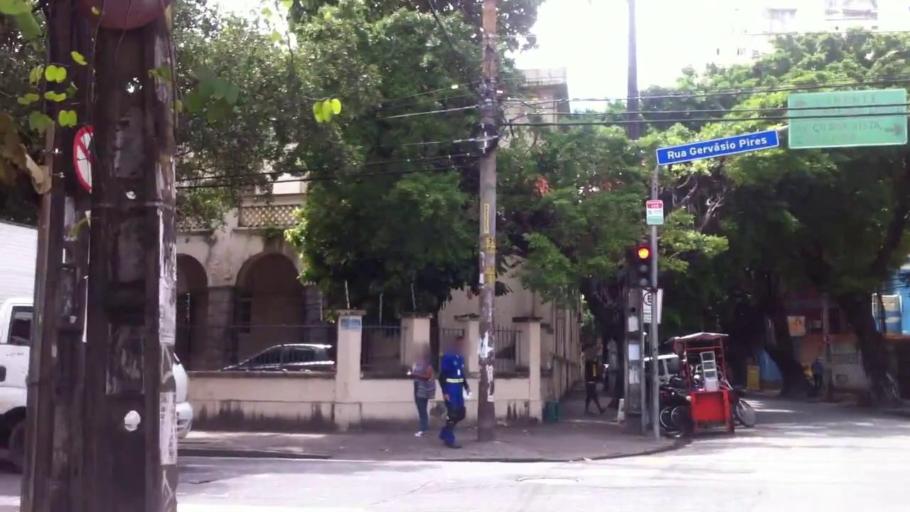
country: BR
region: Pernambuco
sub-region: Recife
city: Recife
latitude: -8.0584
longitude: -34.8853
